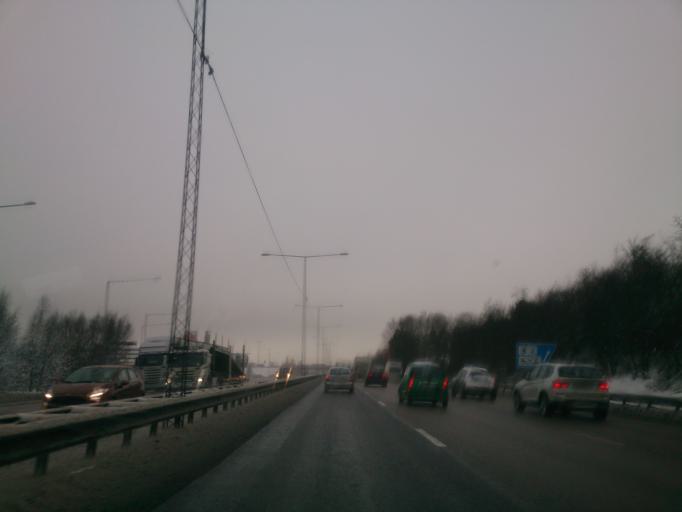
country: SE
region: Stockholm
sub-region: Botkyrka Kommun
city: Fittja
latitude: 59.2502
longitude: 17.8512
